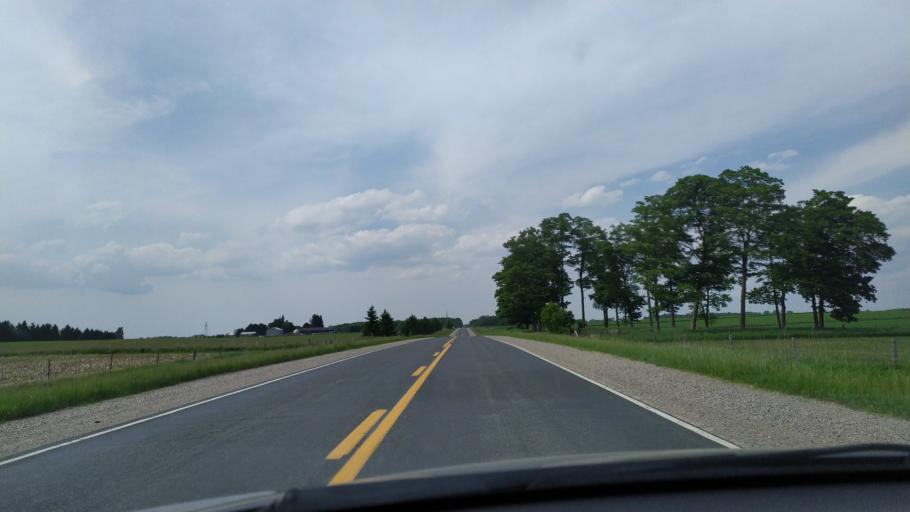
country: CA
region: Ontario
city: Ingersoll
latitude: 43.0312
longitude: -80.9735
